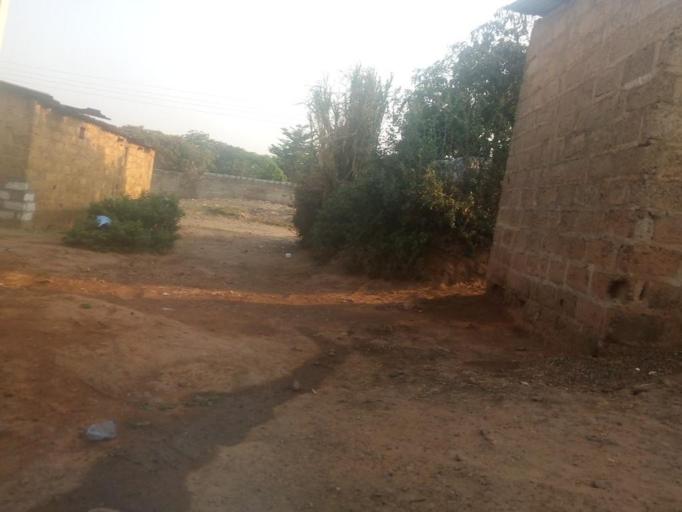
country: ZM
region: Lusaka
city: Lusaka
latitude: -15.4046
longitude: 28.3678
